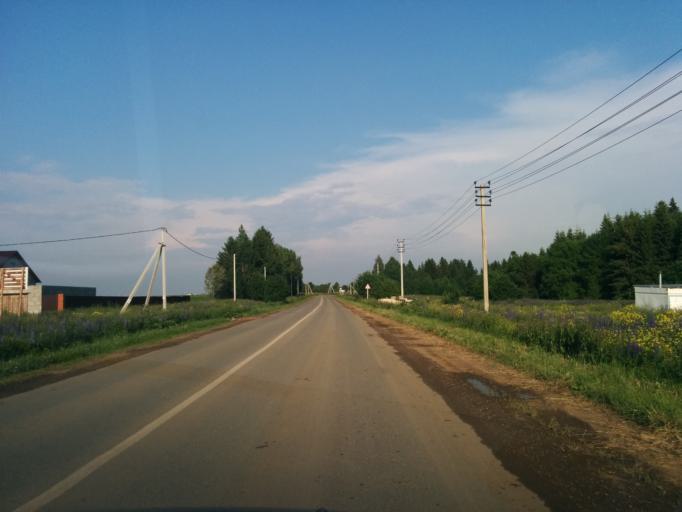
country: RU
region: Perm
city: Polazna
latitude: 58.2373
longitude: 56.2806
